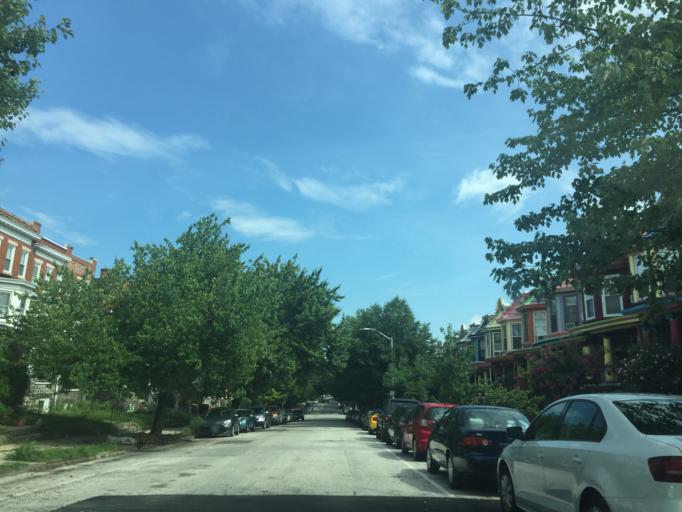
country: US
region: Maryland
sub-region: City of Baltimore
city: Baltimore
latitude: 39.3247
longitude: -76.6133
